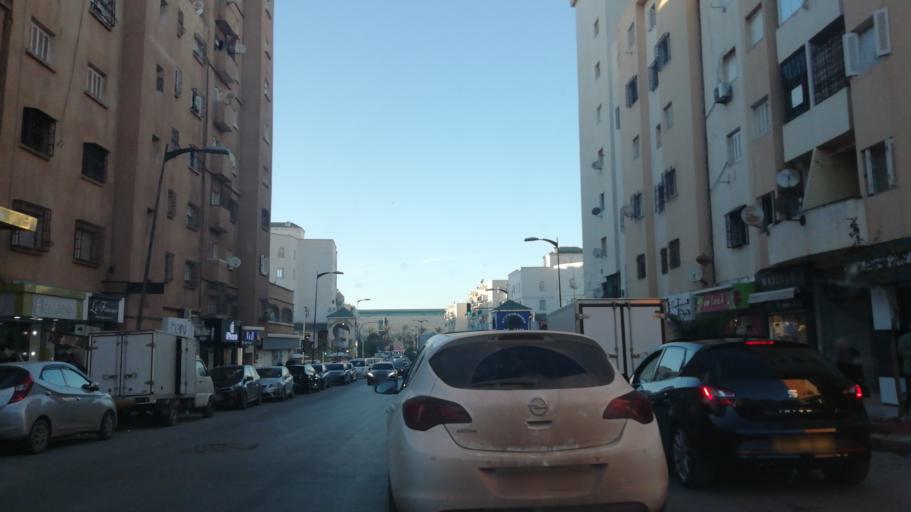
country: DZ
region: Oran
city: Bir el Djir
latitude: 35.7244
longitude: -0.5877
